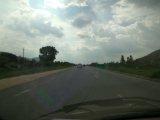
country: IN
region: Karnataka
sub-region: Kolar
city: Kolar
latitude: 13.1255
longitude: 78.0503
